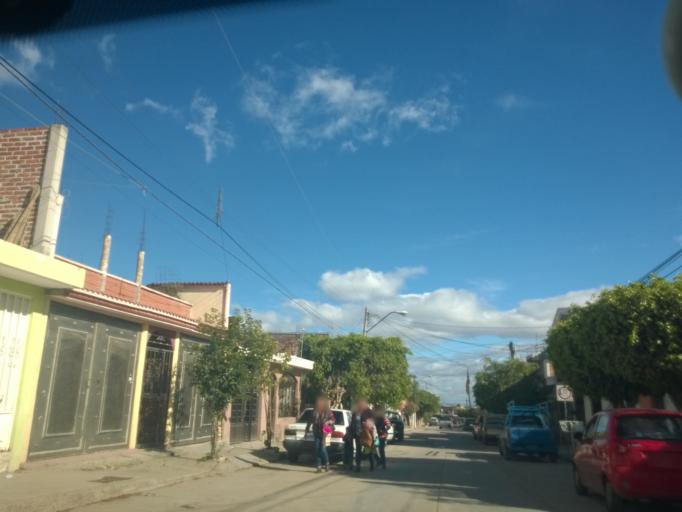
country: MX
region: Guanajuato
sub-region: Leon
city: Ejido la Joya
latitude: 21.1167
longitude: -101.7211
